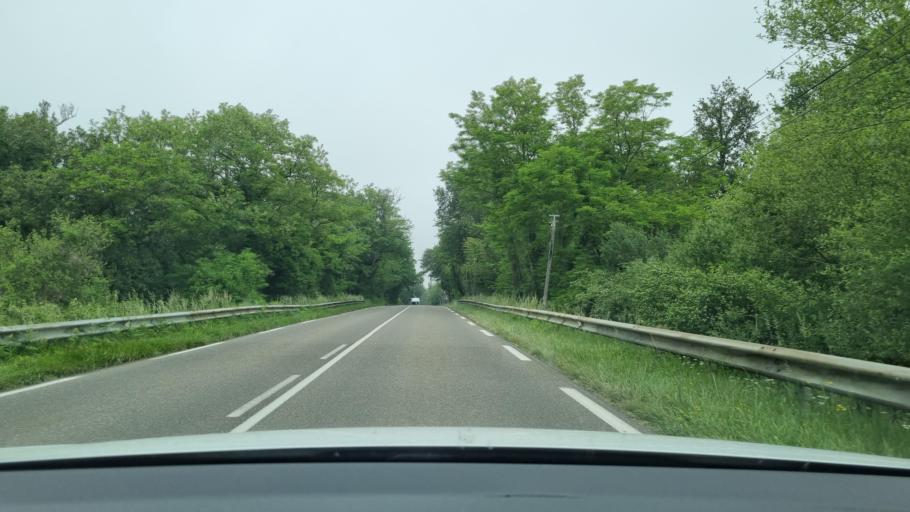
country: FR
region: Aquitaine
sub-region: Departement des Landes
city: Saint-Sever
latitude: 43.7240
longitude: -0.5759
